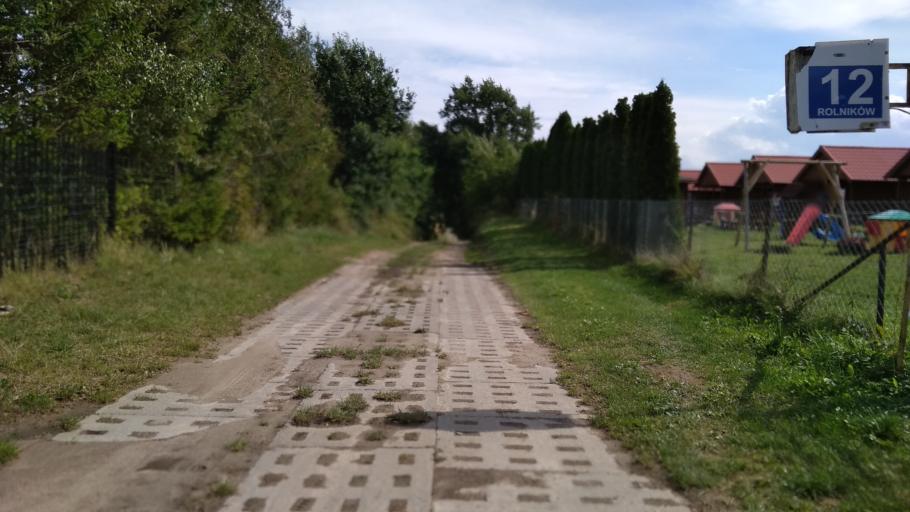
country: PL
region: West Pomeranian Voivodeship
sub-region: Powiat slawienski
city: Darlowo
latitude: 54.5103
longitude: 16.5154
